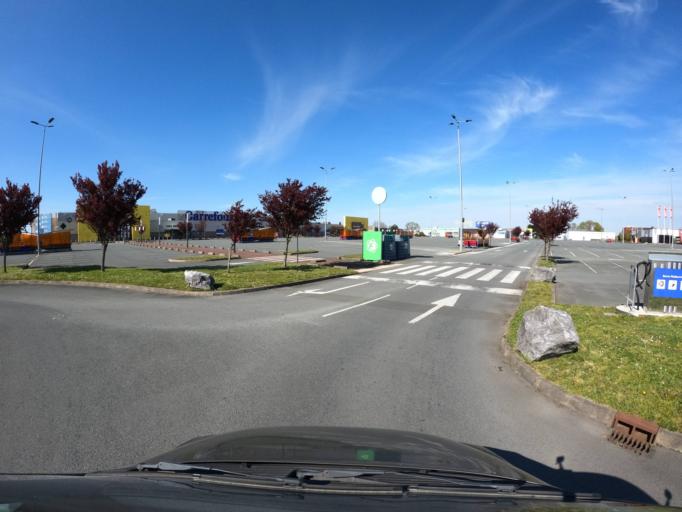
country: FR
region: Pays de la Loire
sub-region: Departement de Maine-et-Loire
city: Mazieres-en-Mauges
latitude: 47.0748
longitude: -0.8431
